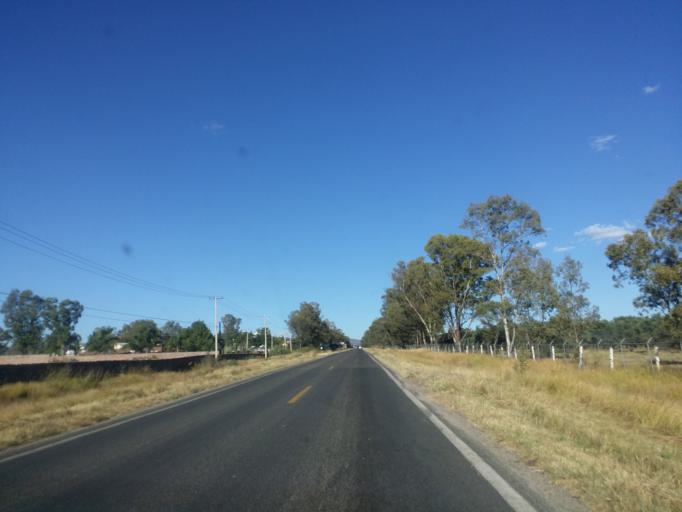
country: MX
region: Guanajuato
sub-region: Silao de la Victoria
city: El Refugio de los Sauces
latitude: 21.0286
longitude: -101.5331
